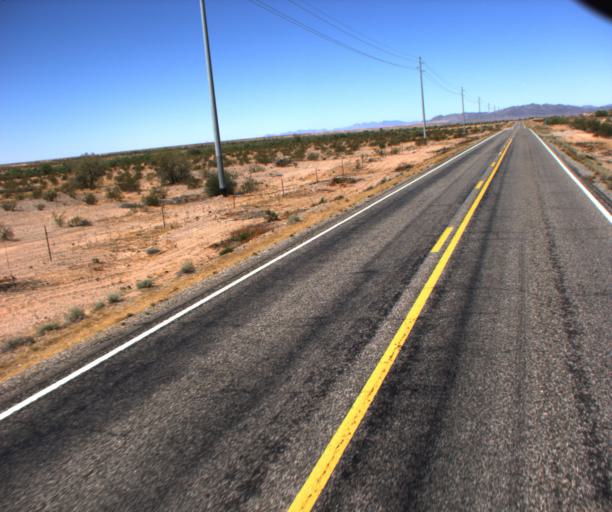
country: US
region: Arizona
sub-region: La Paz County
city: Cienega Springs
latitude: 33.9936
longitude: -114.1139
